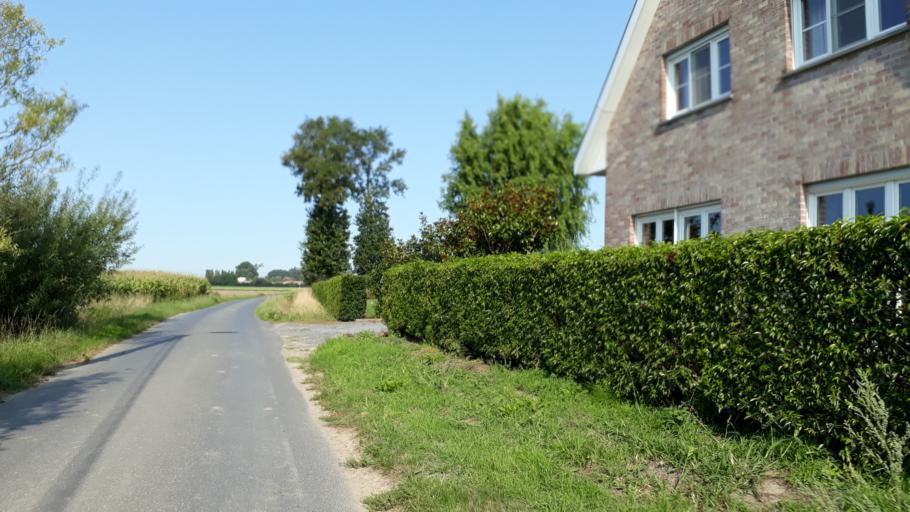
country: BE
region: Flanders
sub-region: Provincie West-Vlaanderen
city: Hooglede
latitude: 51.0173
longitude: 3.0792
